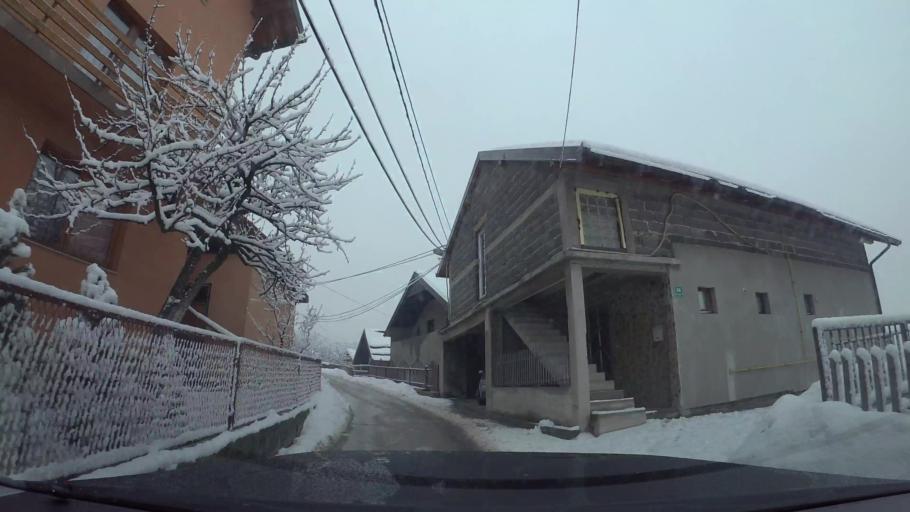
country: BA
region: Federation of Bosnia and Herzegovina
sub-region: Kanton Sarajevo
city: Sarajevo
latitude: 43.8604
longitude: 18.3257
